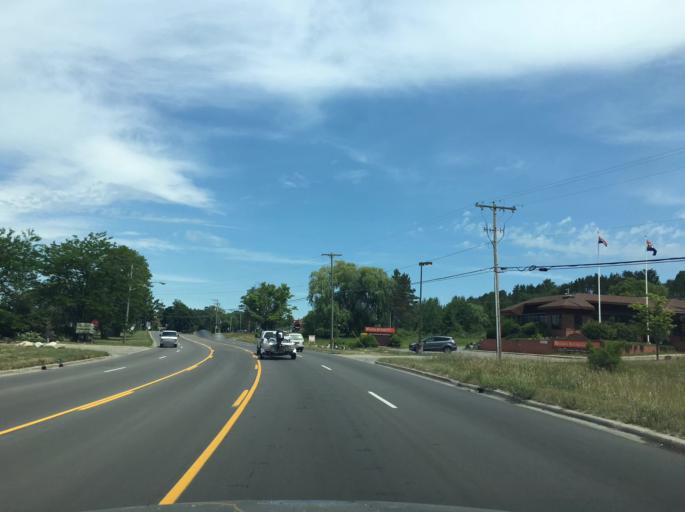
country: US
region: Michigan
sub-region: Grand Traverse County
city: Traverse City
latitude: 44.7675
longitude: -85.5040
